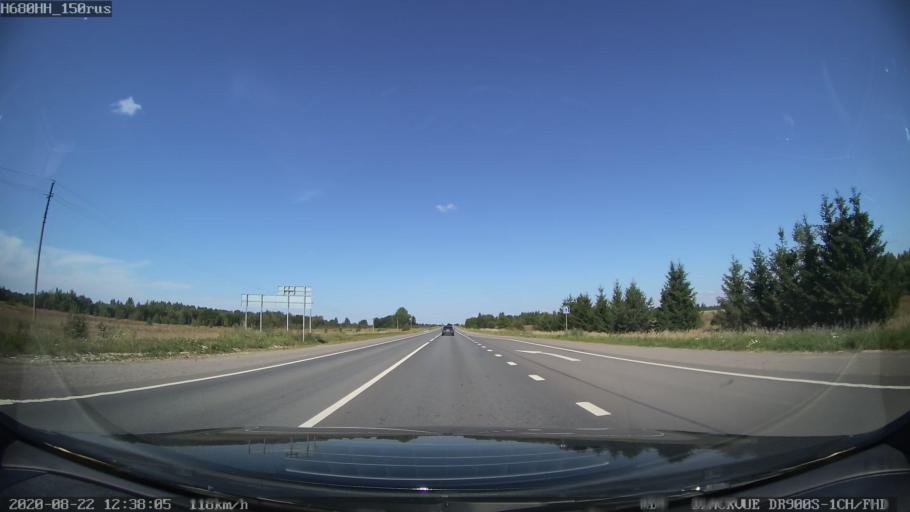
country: RU
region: Tverskaya
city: Rameshki
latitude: 57.3082
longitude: 36.0886
